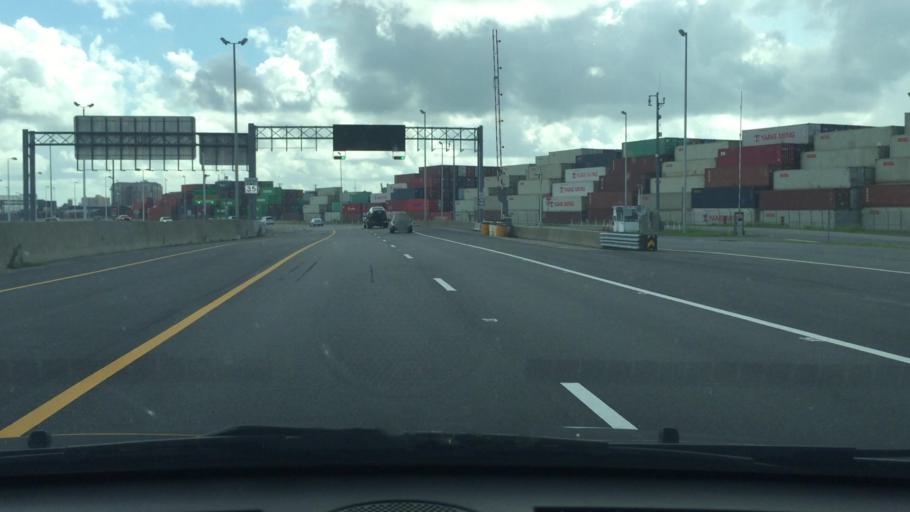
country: US
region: Virginia
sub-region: City of Portsmouth
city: Portsmouth
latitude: 36.8524
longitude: -76.3235
